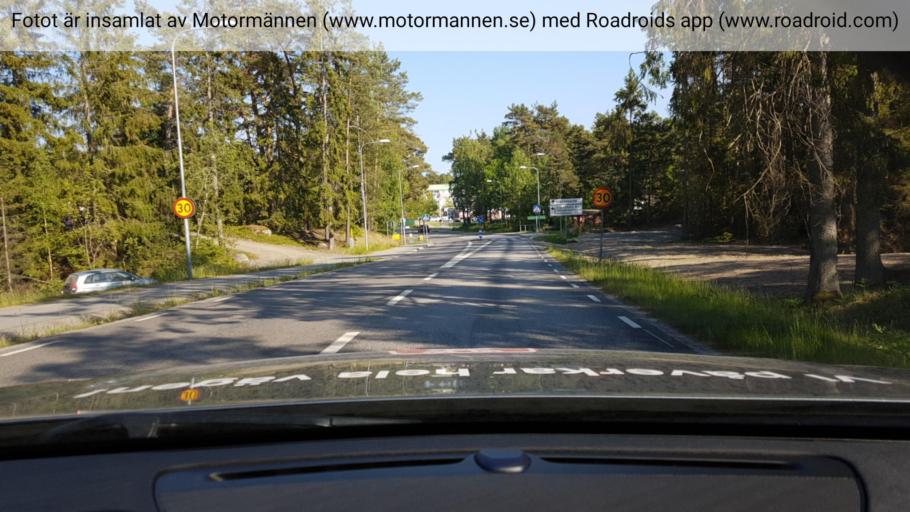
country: SE
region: Stockholm
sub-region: Varmdo Kommun
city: Holo
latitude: 59.2884
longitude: 18.6851
